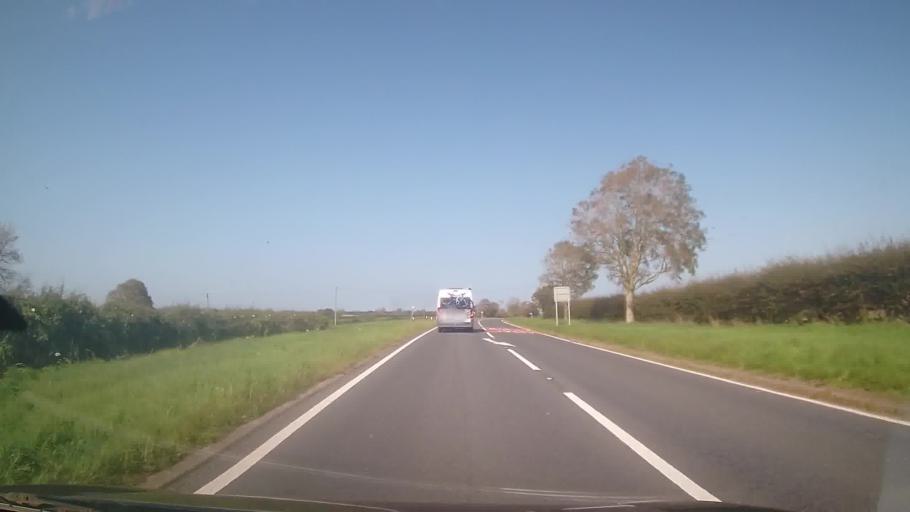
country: GB
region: Wales
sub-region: County of Ceredigion
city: Cardigan
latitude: 52.0392
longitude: -4.6966
